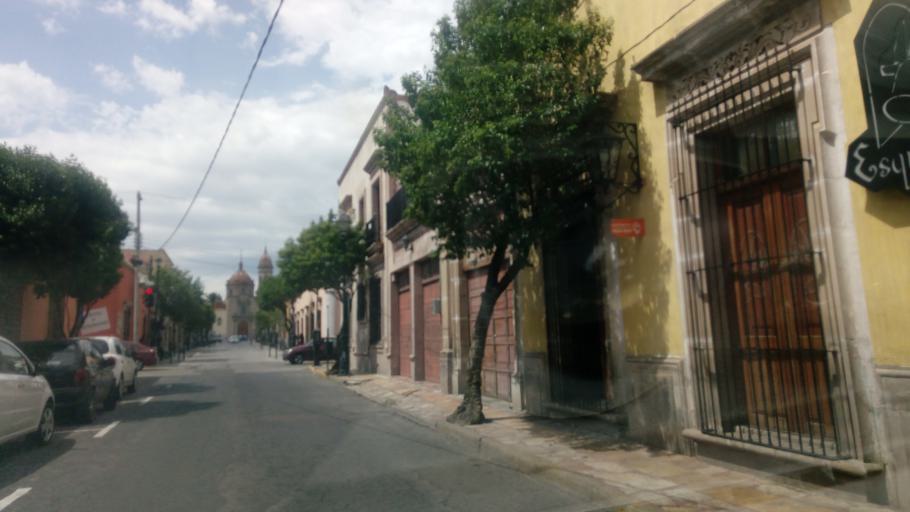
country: MX
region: Durango
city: Victoria de Durango
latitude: 24.0225
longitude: -104.6732
